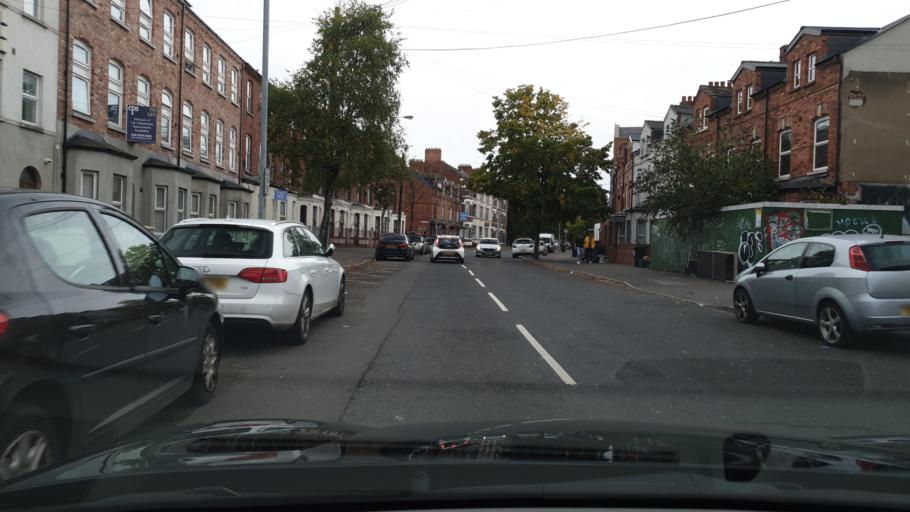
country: GB
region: Northern Ireland
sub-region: City of Belfast
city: Belfast
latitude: 54.5864
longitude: -5.9244
